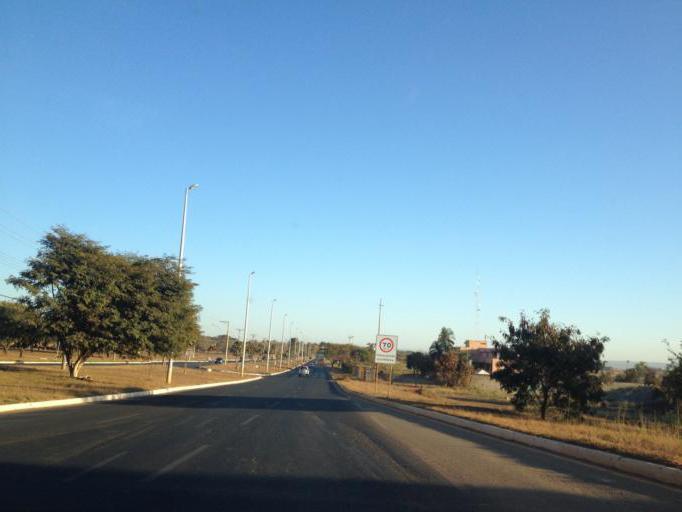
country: BR
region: Federal District
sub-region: Brasilia
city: Brasilia
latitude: -15.7704
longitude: -47.9103
